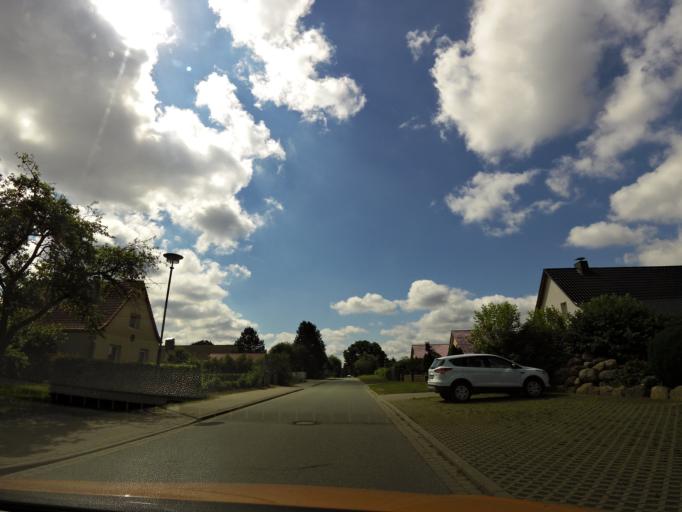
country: DE
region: Mecklenburg-Vorpommern
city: Plau am See
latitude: 53.4467
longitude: 12.2825
